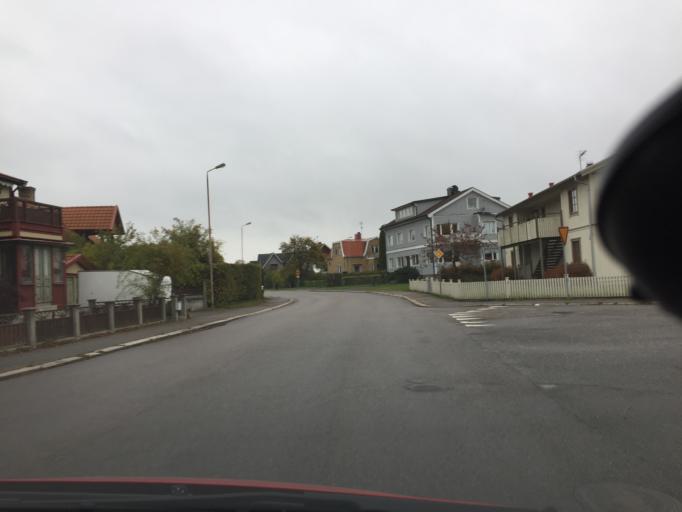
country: SE
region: Vaestra Goetaland
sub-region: Trollhattan
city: Trollhattan
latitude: 58.2898
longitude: 12.3022
